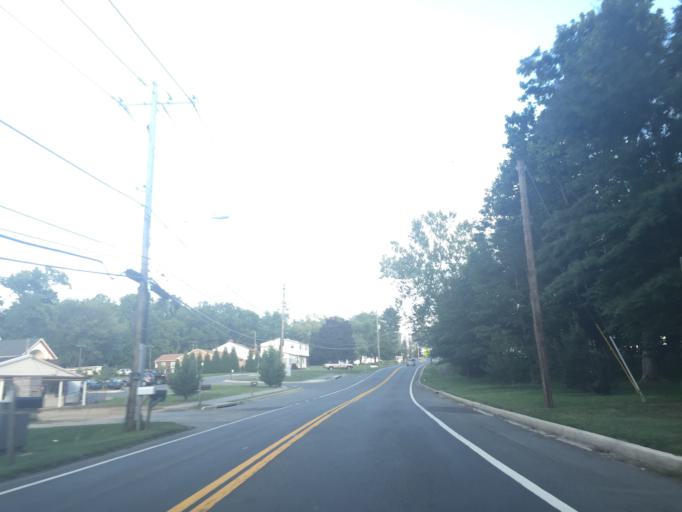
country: US
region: Maryland
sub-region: Montgomery County
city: Rossmoor
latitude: 39.1109
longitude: -77.0840
